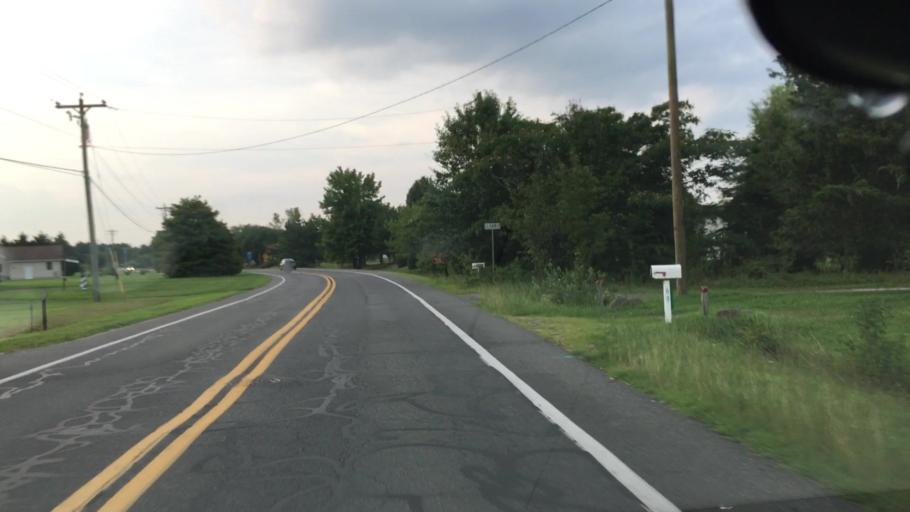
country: US
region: Delaware
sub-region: Sussex County
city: Ocean View
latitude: 38.5306
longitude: -75.0865
